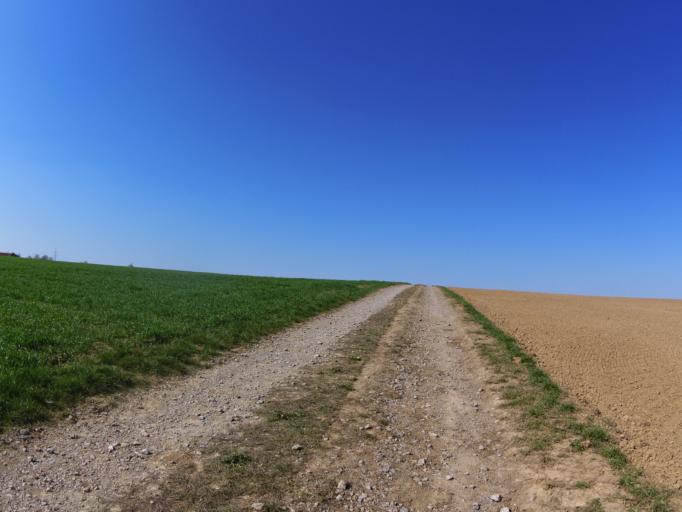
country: DE
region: Bavaria
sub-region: Regierungsbezirk Unterfranken
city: Biebelried
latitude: 49.8172
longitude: 10.1018
